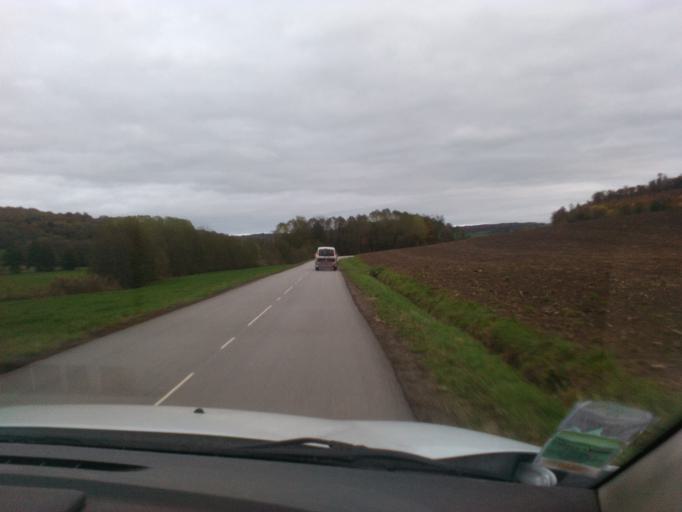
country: FR
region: Lorraine
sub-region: Departement des Vosges
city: Charmes
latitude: 48.2745
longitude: 6.2407
